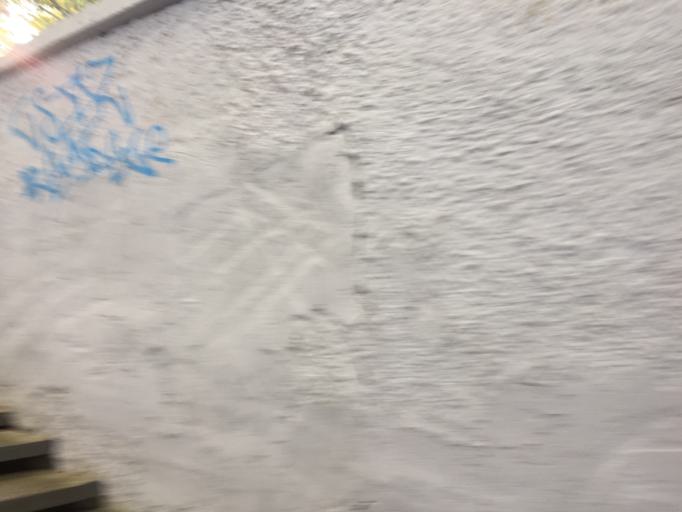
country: RU
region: Kaliningrad
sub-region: Gorod Svetlogorsk
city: Svetlogorsk
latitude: 54.9476
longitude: 20.1652
